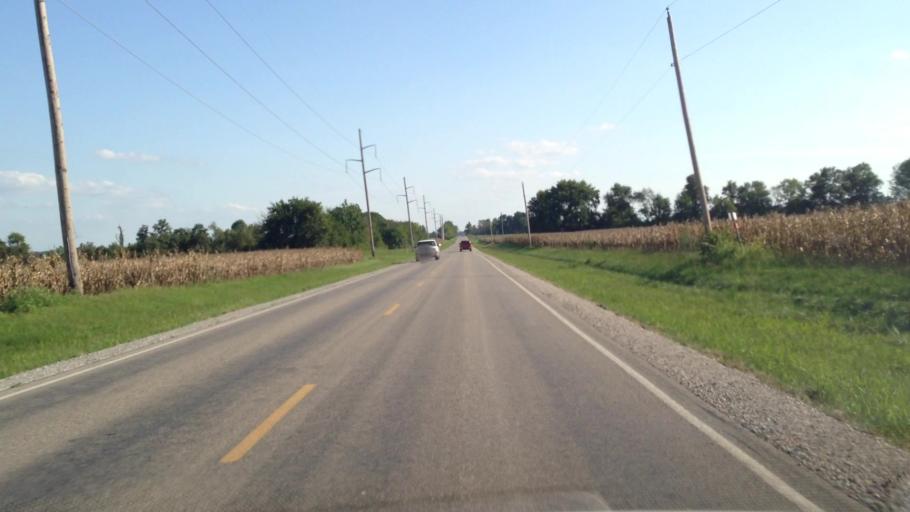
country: US
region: Kansas
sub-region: Crawford County
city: Pittsburg
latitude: 37.3736
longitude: -94.6314
